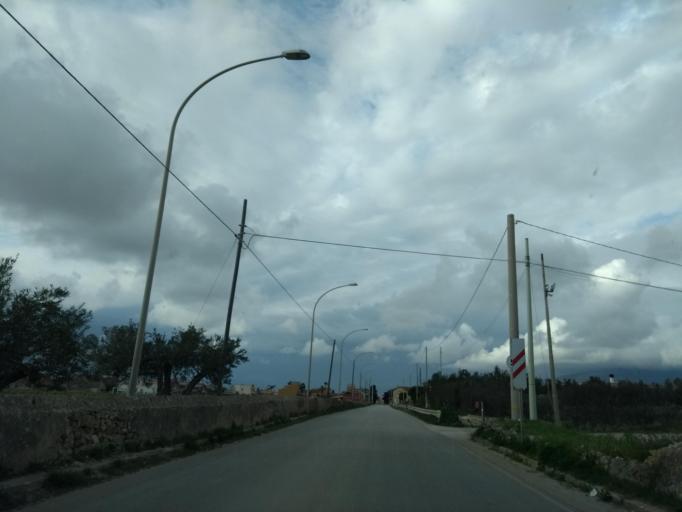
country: IT
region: Sicily
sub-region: Trapani
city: Marausa
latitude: 37.9597
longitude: 12.5175
